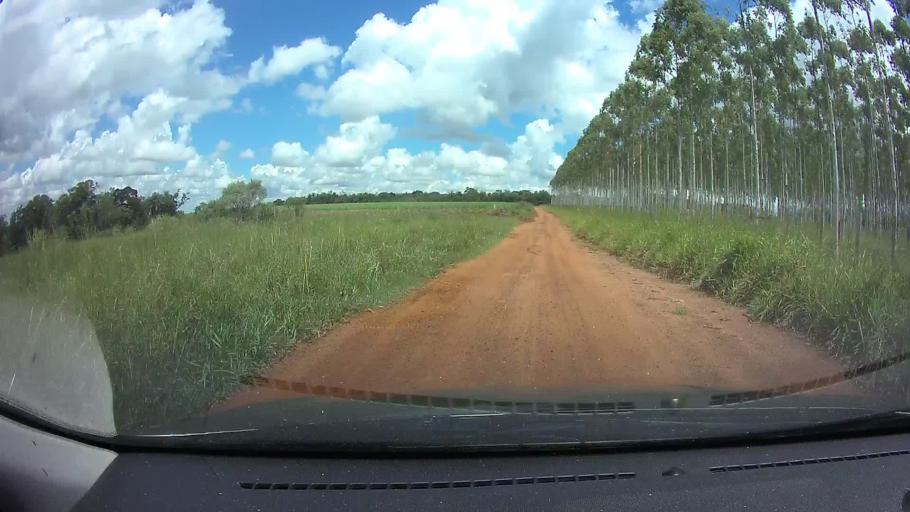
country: PY
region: Paraguari
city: La Colmena
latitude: -25.9650
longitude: -56.7329
